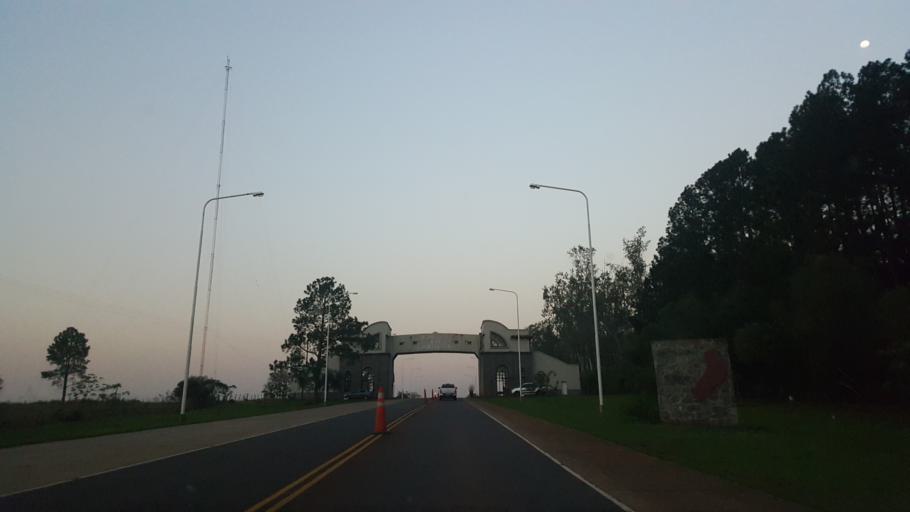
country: PY
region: Itapua
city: San Juan del Parana
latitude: -27.4544
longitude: -56.0496
